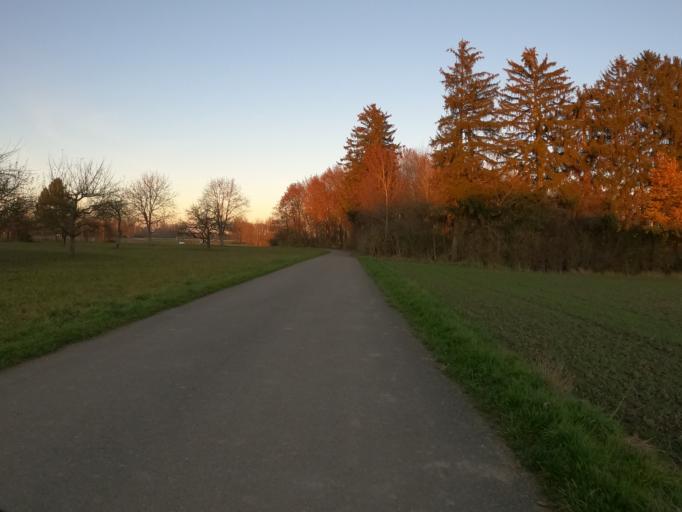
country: DE
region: Bavaria
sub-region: Swabia
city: Holzheim
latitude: 48.4182
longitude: 10.0740
